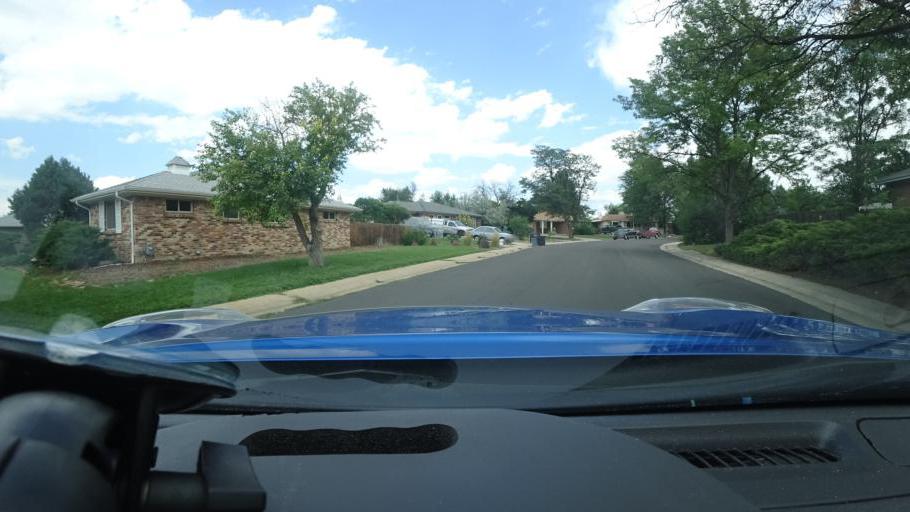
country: US
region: Colorado
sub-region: Adams County
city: Aurora
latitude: 39.7230
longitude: -104.8363
